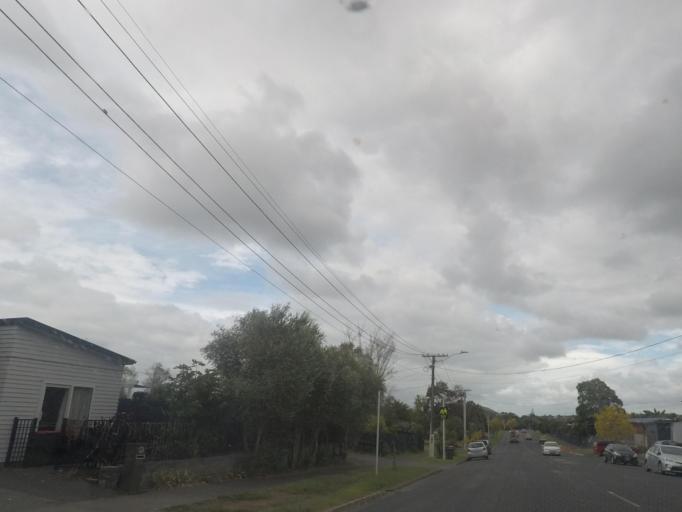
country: NZ
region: Auckland
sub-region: Auckland
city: Tamaki
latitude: -36.8771
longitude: 174.8703
